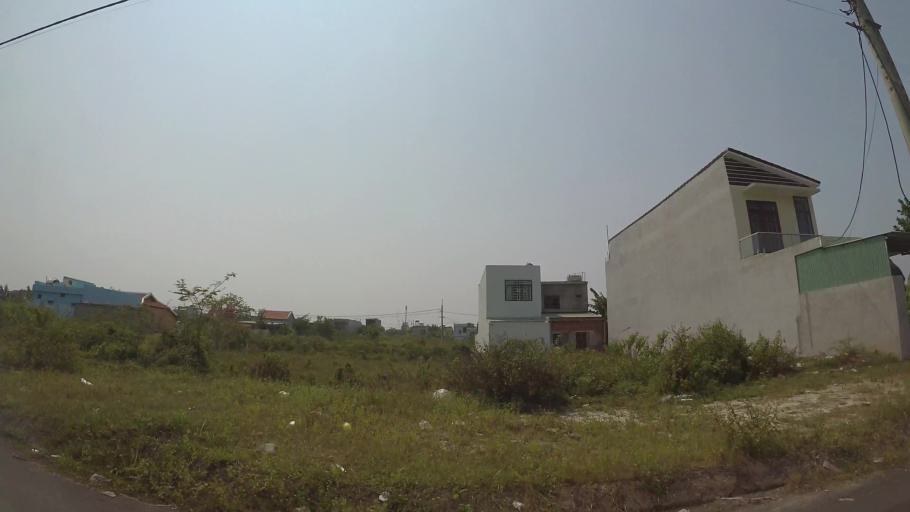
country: VN
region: Da Nang
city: Cam Le
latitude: 15.9857
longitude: 108.2112
